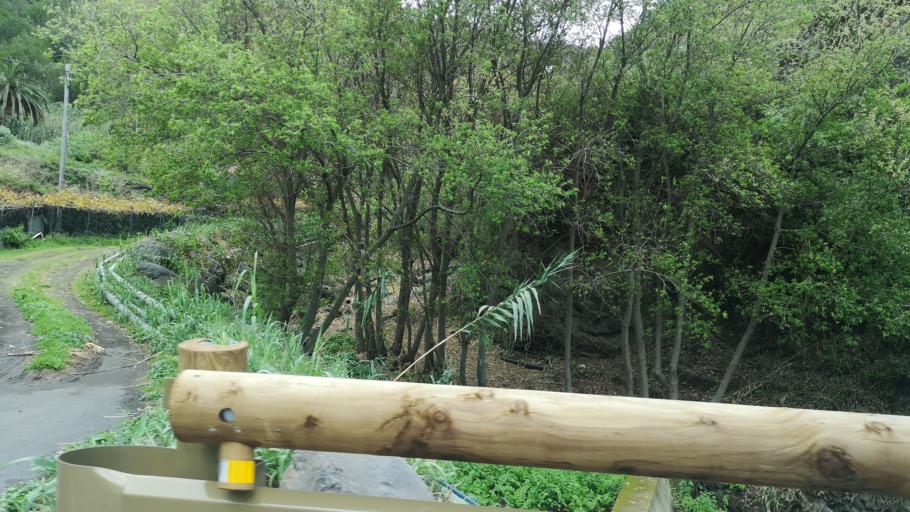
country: ES
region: Canary Islands
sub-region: Provincia de Santa Cruz de Tenerife
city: Hermigua
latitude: 28.1411
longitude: -17.1947
